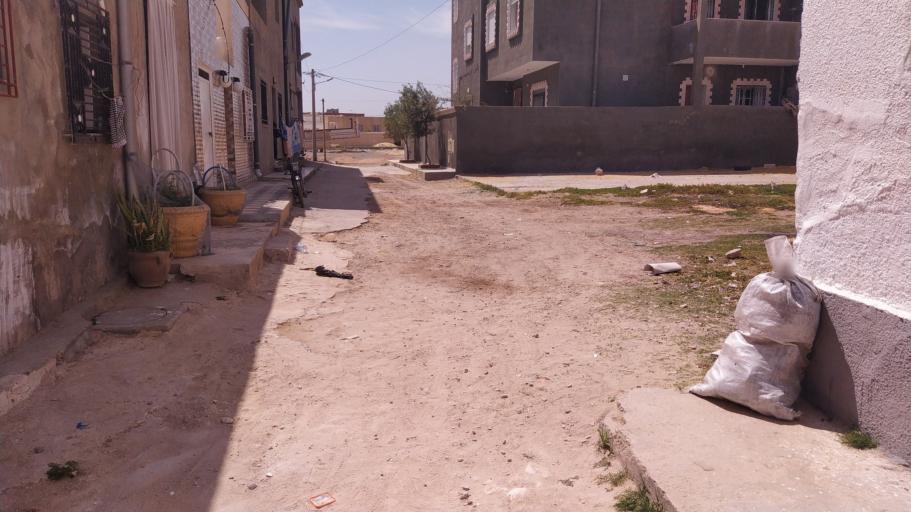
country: TN
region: Al Mahdiyah
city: Zouila
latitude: 35.5040
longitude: 11.0403
